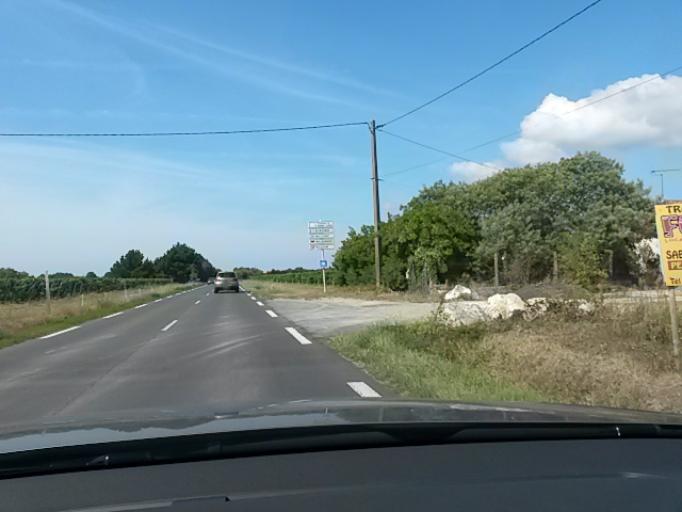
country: FR
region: Poitou-Charentes
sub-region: Departement de la Charente-Maritime
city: Saint-Denis-d'Oleron
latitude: 45.9607
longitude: -1.3417
